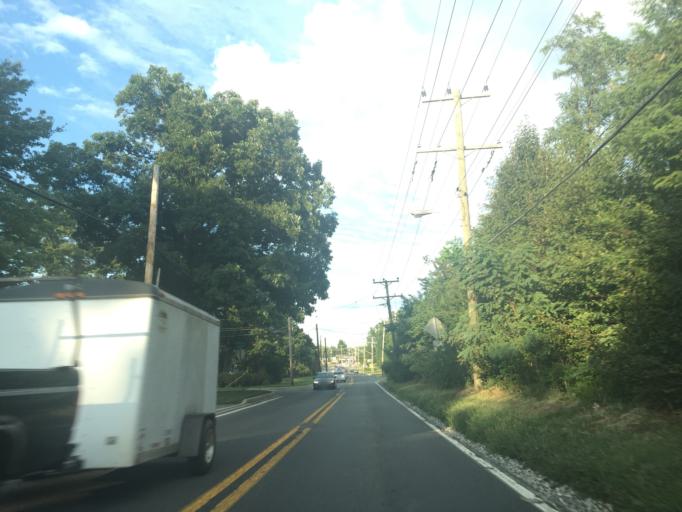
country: US
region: Maryland
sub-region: Montgomery County
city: Burtonsville
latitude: 39.1067
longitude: -76.9404
